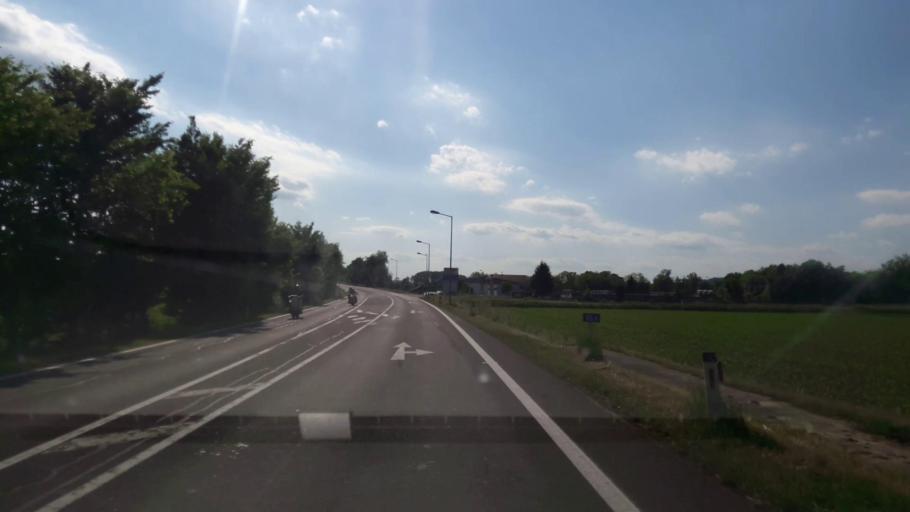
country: AT
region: Styria
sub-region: Politischer Bezirk Suedoststeiermark
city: Fehring
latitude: 46.9431
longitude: 16.0197
